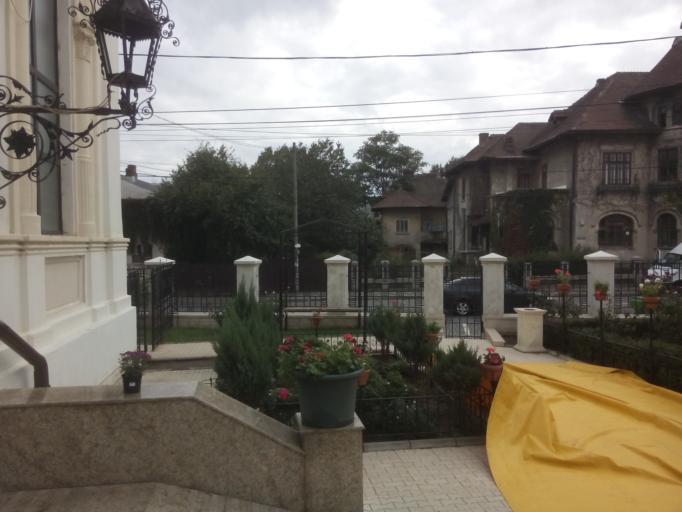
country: RO
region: Prahova
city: Ploiesti
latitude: 44.9434
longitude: 26.0294
